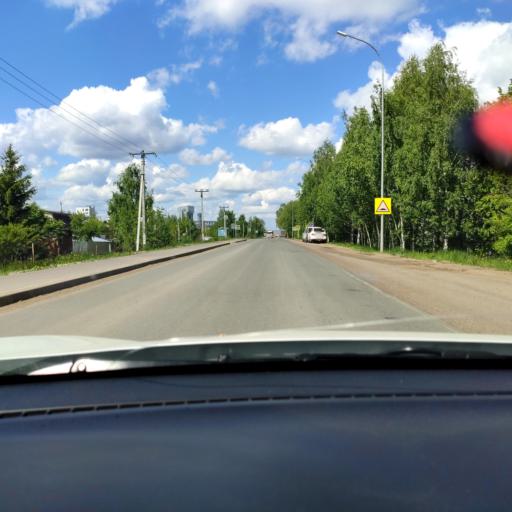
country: RU
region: Tatarstan
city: Stolbishchi
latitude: 55.6990
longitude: 49.1848
